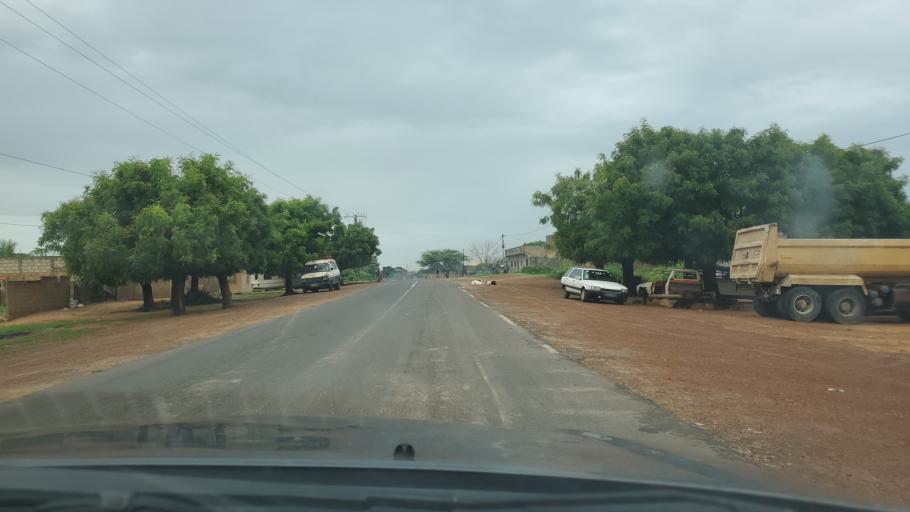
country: SN
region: Thies
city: Mekhe
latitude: 15.1289
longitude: -16.8620
